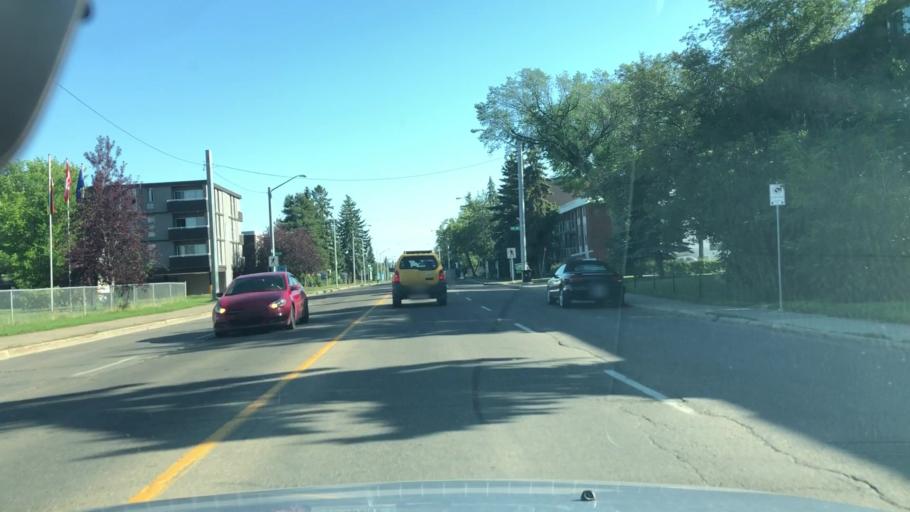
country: CA
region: Alberta
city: Edmonton
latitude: 53.5642
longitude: -113.5360
